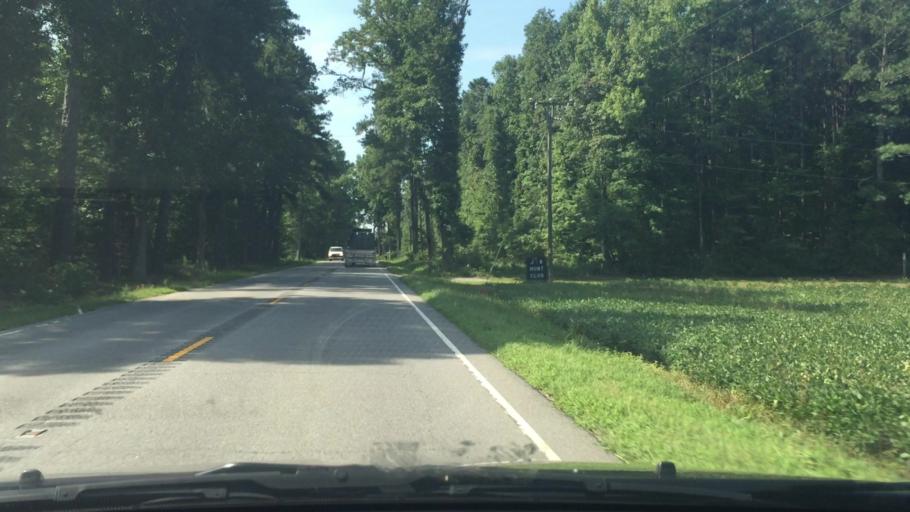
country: US
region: Virginia
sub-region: Sussex County
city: Sussex
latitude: 36.8945
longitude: -77.1527
